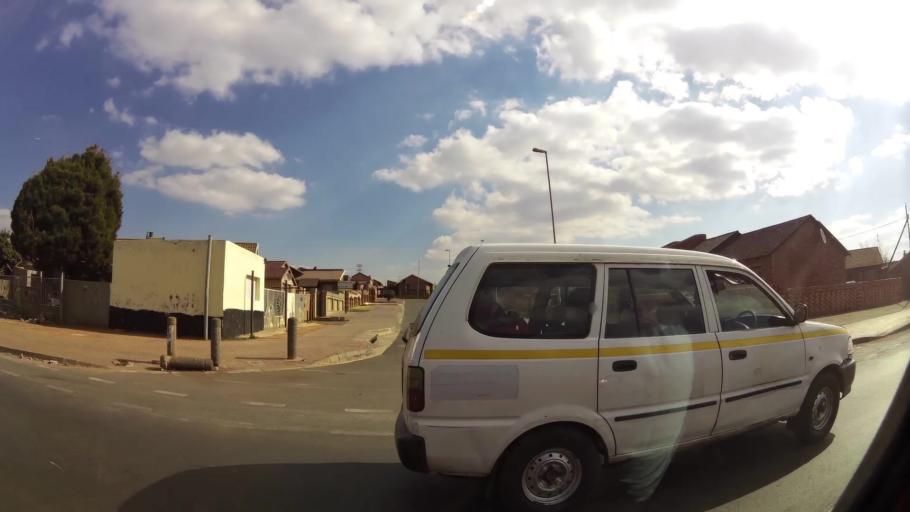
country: ZA
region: Gauteng
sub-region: Ekurhuleni Metropolitan Municipality
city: Tembisa
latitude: -25.9938
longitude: 28.2452
